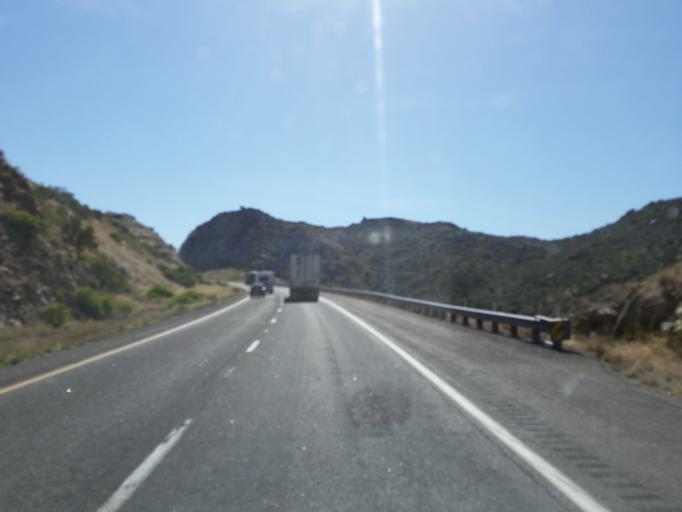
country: US
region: Arizona
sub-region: Mohave County
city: Peach Springs
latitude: 35.1704
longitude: -113.5142
